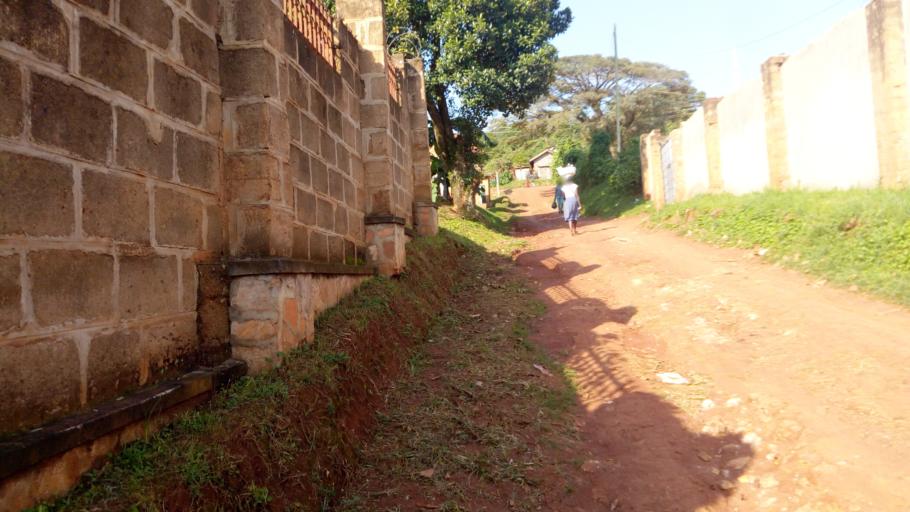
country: UG
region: Central Region
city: Kampala Central Division
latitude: 0.3400
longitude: 32.5603
